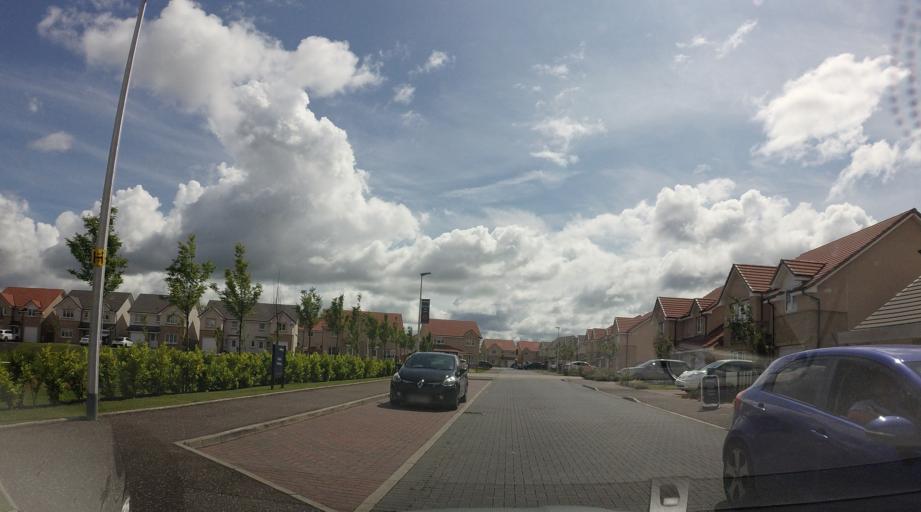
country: GB
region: Scotland
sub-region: West Lothian
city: Broxburn
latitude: 55.9341
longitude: -3.4588
